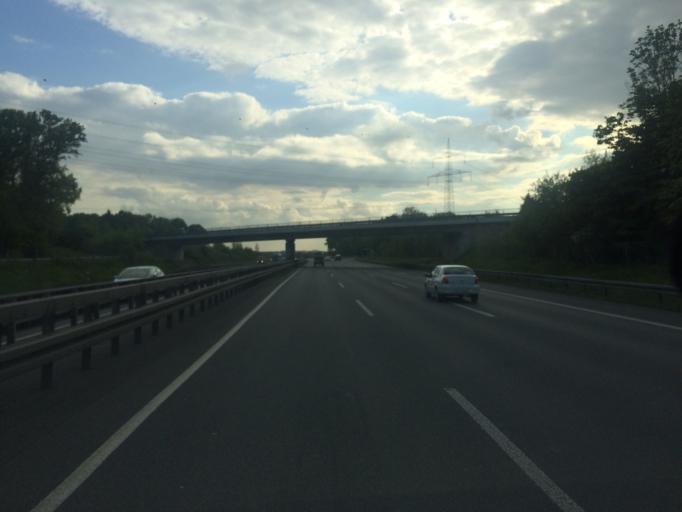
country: DE
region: North Rhine-Westphalia
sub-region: Regierungsbezirk Arnsberg
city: Welver
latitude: 51.6728
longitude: 7.9404
